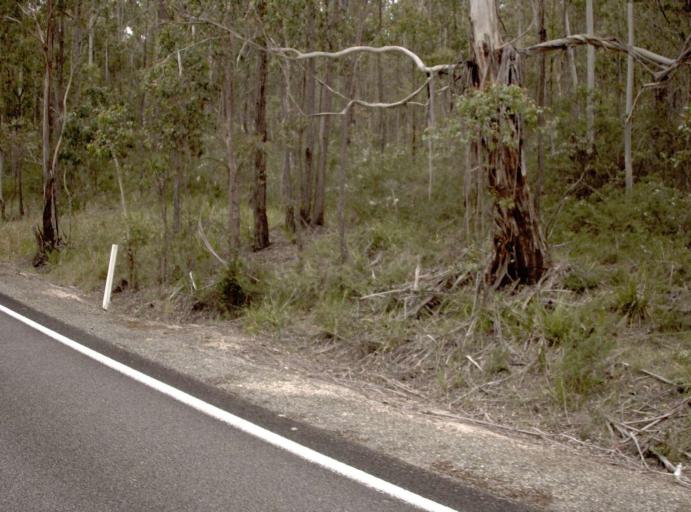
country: AU
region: New South Wales
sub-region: Bombala
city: Bombala
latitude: -37.2801
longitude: 149.2234
